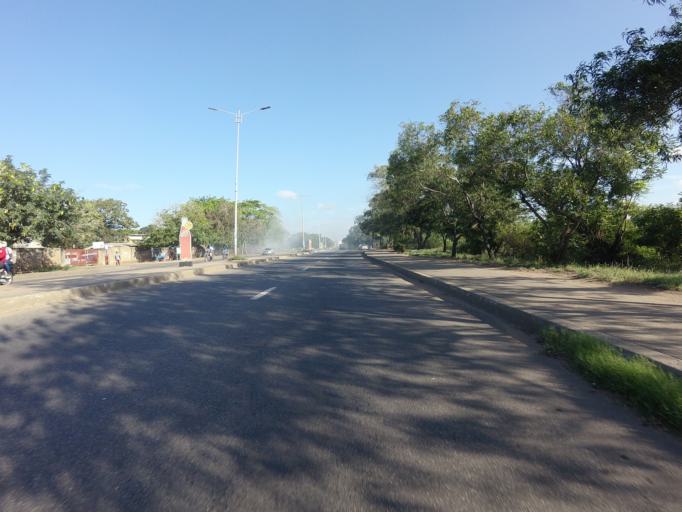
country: GH
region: Greater Accra
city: Accra
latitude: 5.5425
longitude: -0.2261
